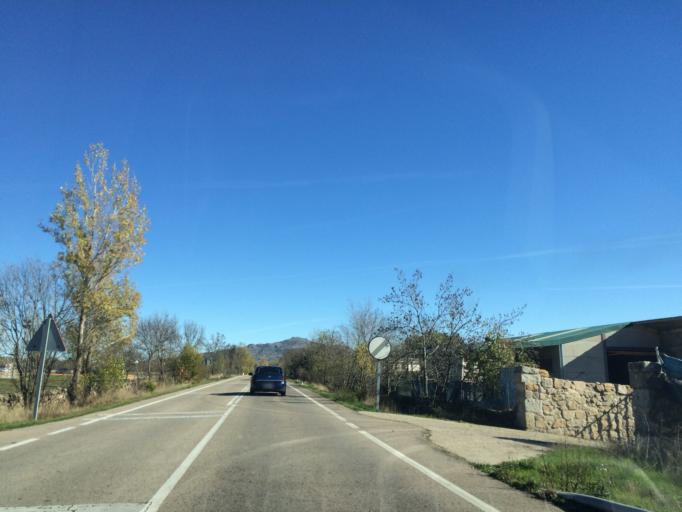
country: ES
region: Madrid
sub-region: Provincia de Madrid
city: Manzanares el Real
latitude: 40.7394
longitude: -3.8125
